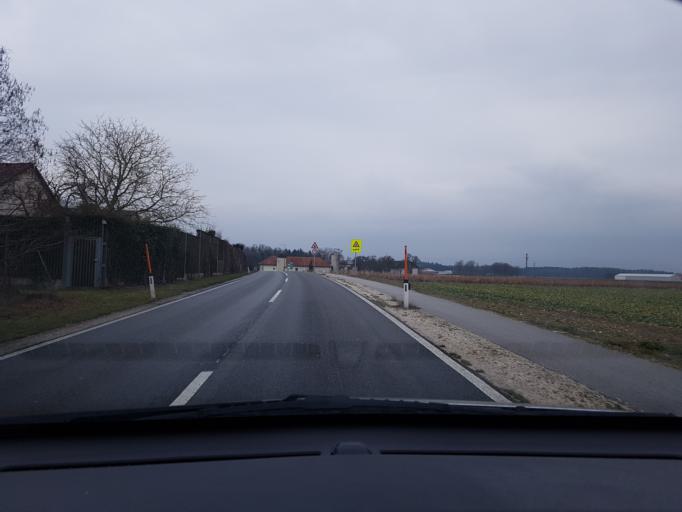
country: AT
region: Upper Austria
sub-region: Steyr Stadt
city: Steyr
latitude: 48.0827
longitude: 14.3702
